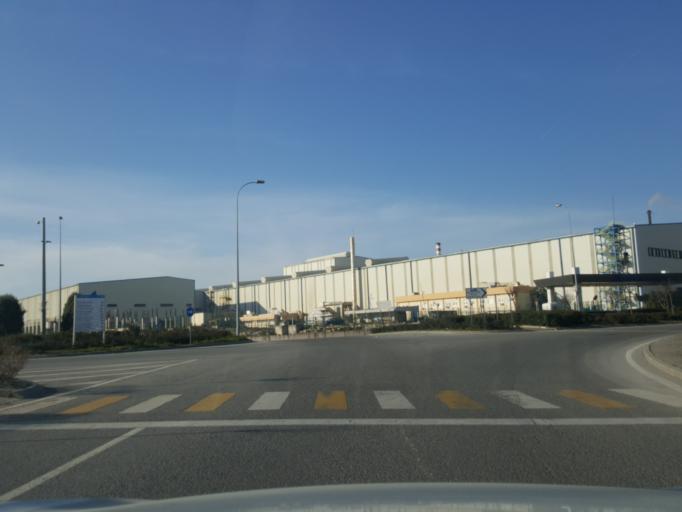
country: TR
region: Kocaeli
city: Tavsanli
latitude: 40.8304
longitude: 29.5585
